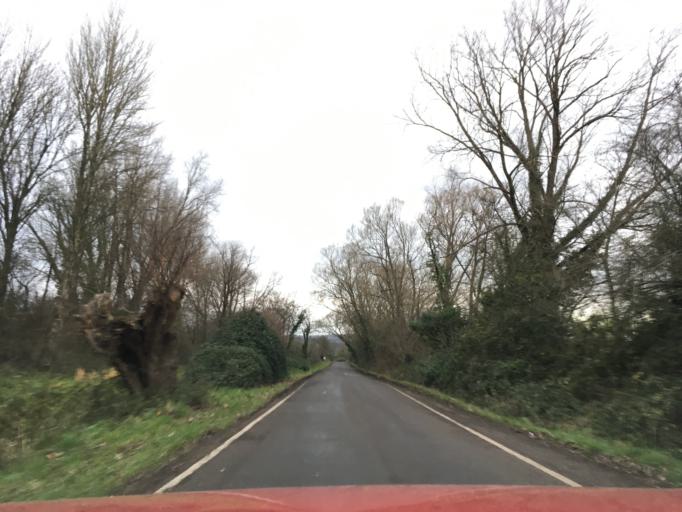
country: GB
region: Wales
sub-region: Newport
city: Bishton
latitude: 51.5772
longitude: -2.8707
